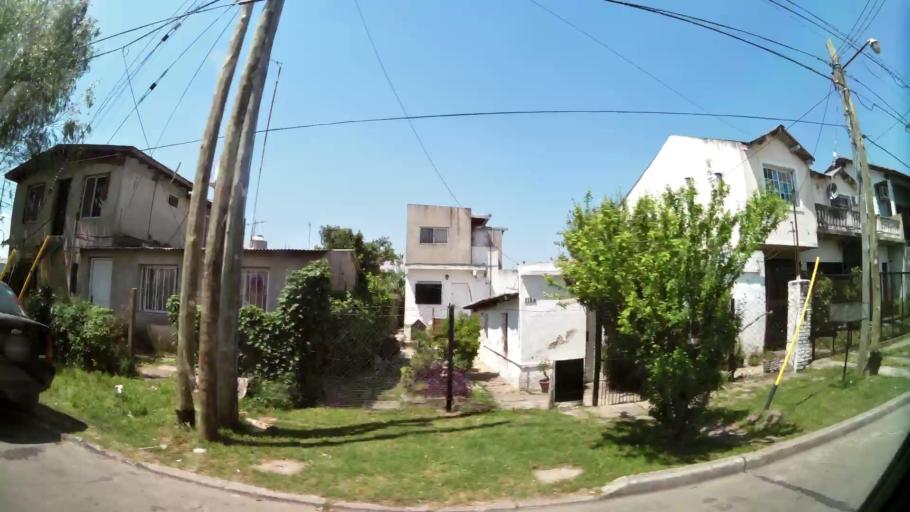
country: AR
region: Buenos Aires
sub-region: Partido de Tigre
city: Tigre
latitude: -34.4555
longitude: -58.5808
